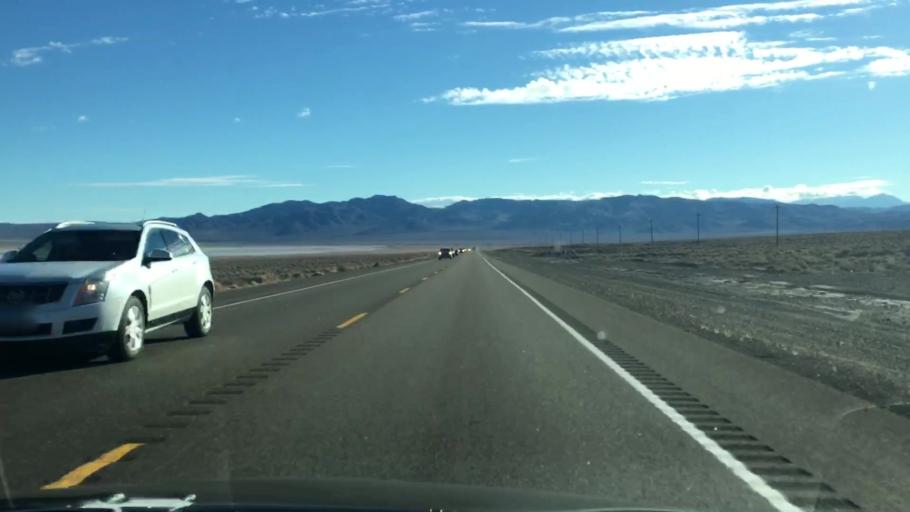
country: US
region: Nevada
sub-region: Mineral County
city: Hawthorne
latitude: 38.3210
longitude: -118.1028
